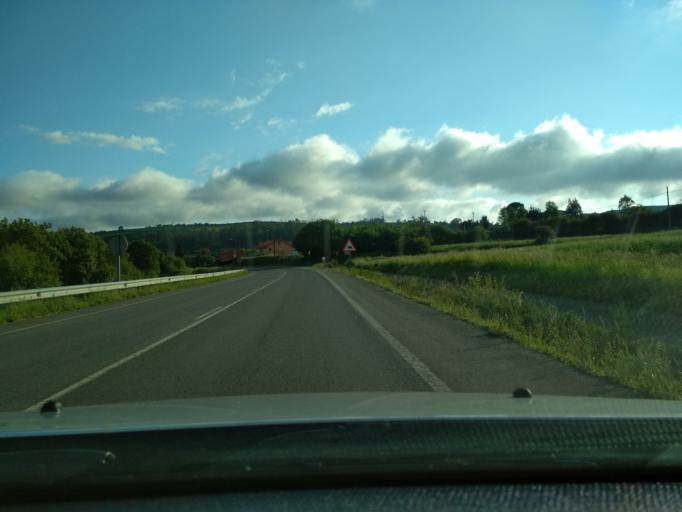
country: ES
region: Galicia
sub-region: Provincia da Coruna
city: Mazaricos
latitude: 42.9562
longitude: -8.9282
